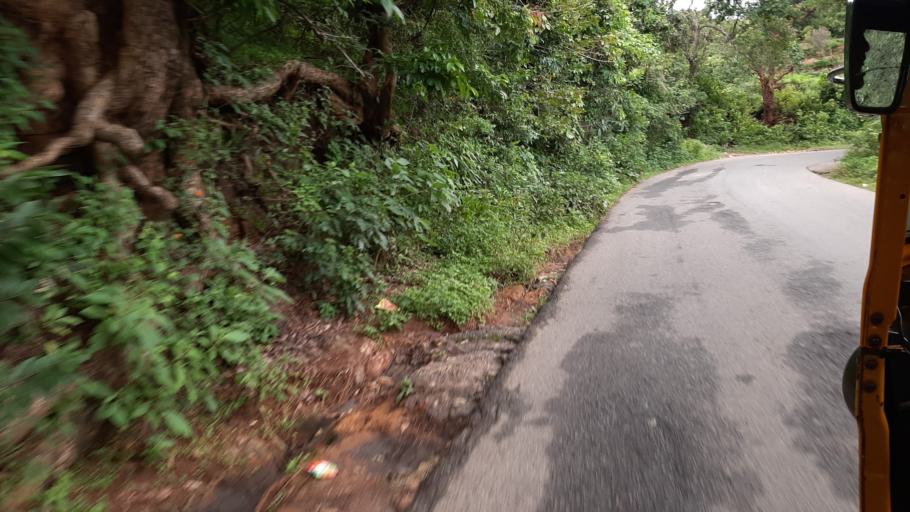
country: IN
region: Andhra Pradesh
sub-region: Vizianagaram District
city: Salur
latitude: 18.2432
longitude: 83.0265
